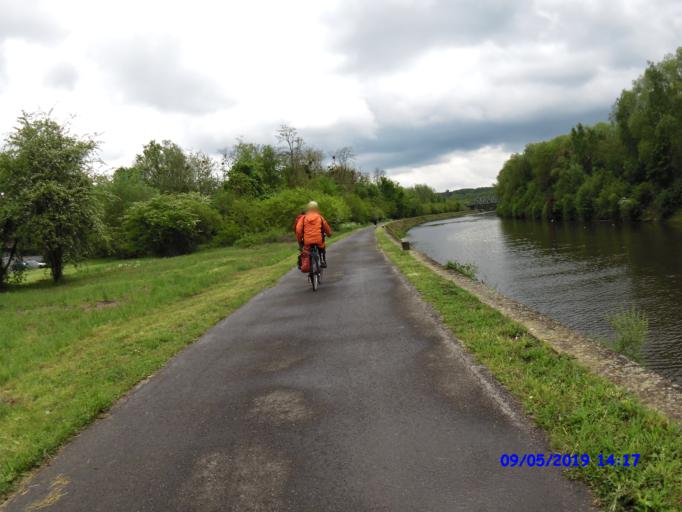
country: BE
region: Wallonia
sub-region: Province du Hainaut
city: Aiseau
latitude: 50.4331
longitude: 4.5894
